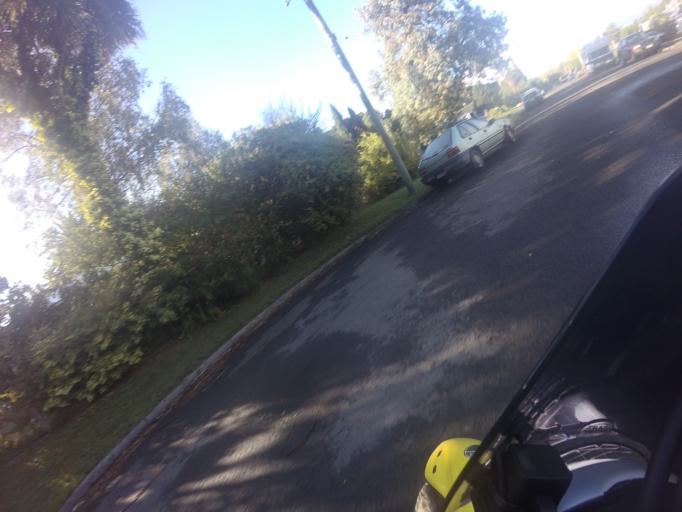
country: NZ
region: Gisborne
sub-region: Gisborne District
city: Gisborne
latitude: -38.6657
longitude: 178.0589
